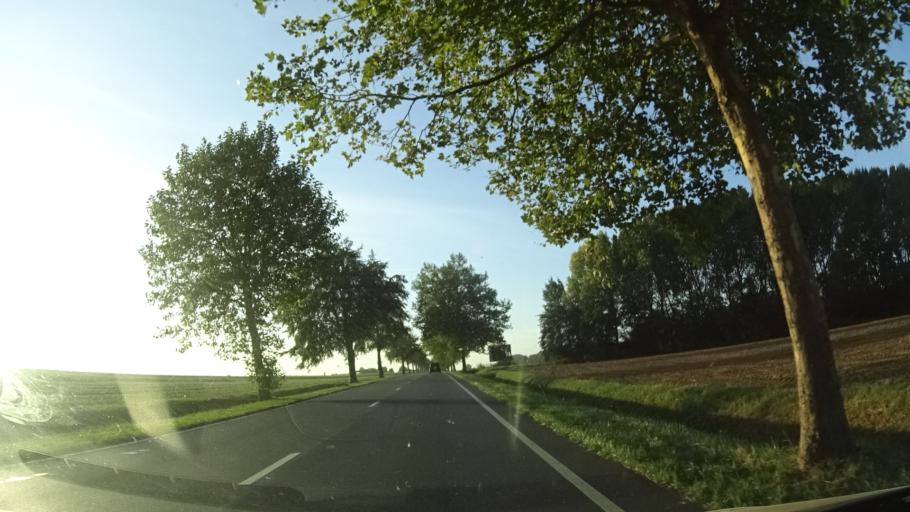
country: BE
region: Wallonia
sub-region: Province du Hainaut
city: Estinnes-au-Val
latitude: 50.3697
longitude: 4.0461
